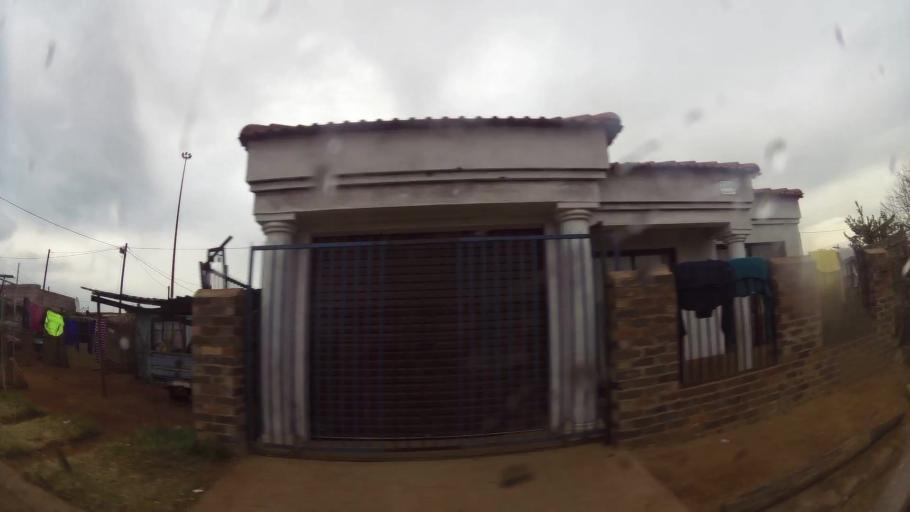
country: ZA
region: Gauteng
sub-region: Ekurhuleni Metropolitan Municipality
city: Germiston
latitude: -26.3696
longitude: 28.1687
